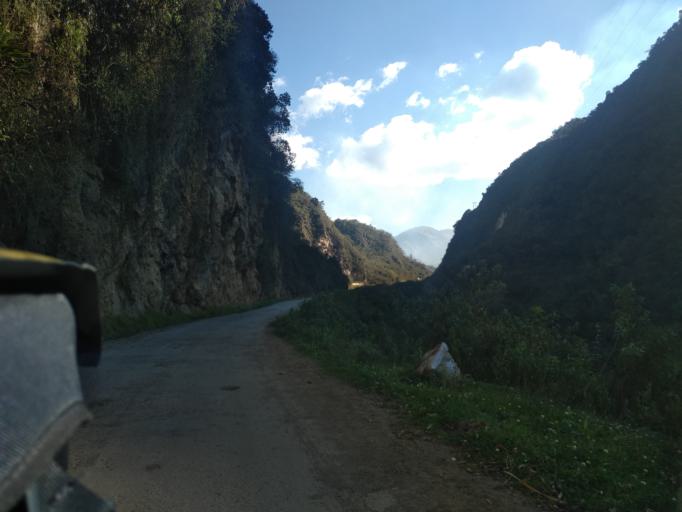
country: PE
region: Amazonas
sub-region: Provincia de Chachapoyas
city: Montevideo
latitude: -6.7215
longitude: -77.8238
